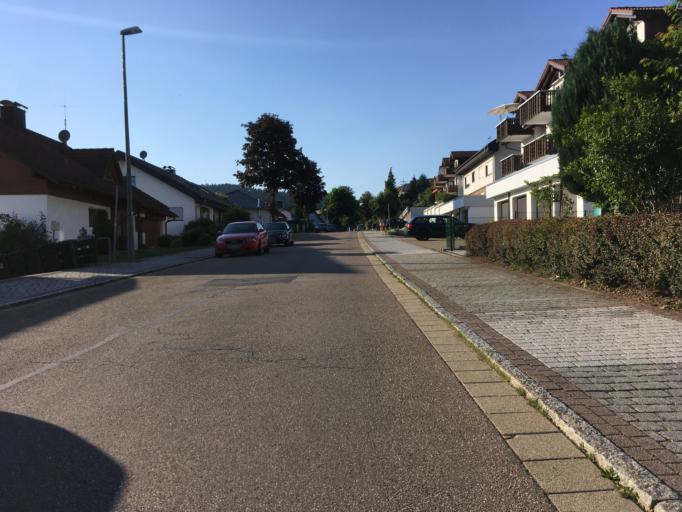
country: DE
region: Baden-Wuerttemberg
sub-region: Freiburg Region
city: Titisee-Neustadt
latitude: 47.9152
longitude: 8.2214
